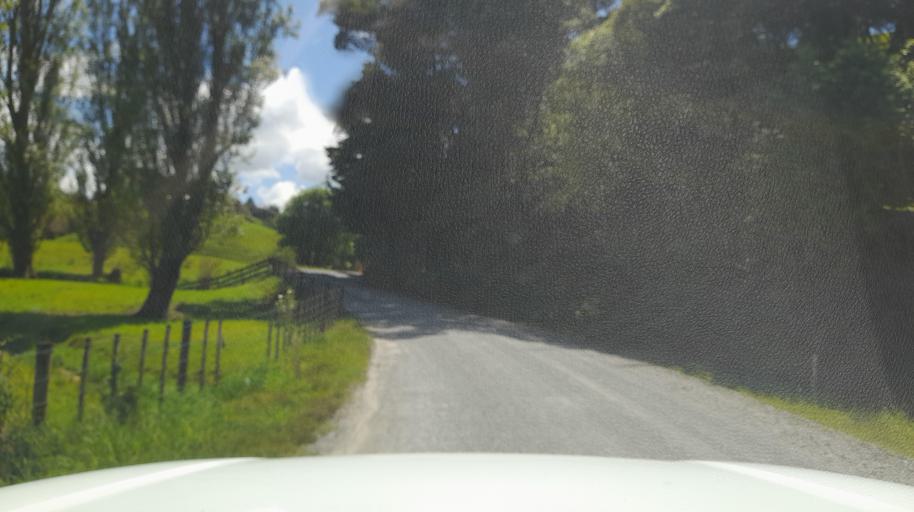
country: NZ
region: Northland
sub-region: Far North District
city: Kaitaia
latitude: -35.1201
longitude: 173.3980
